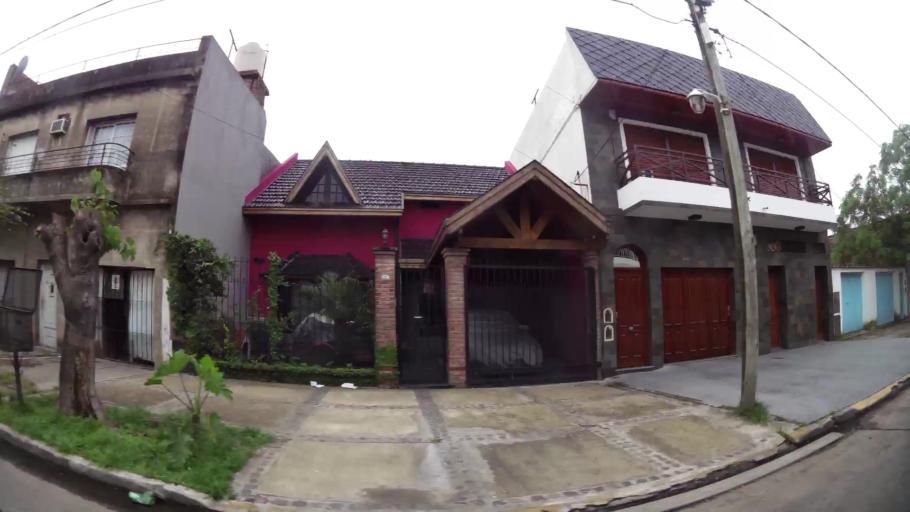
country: AR
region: Buenos Aires
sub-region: Partido de Lanus
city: Lanus
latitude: -34.7110
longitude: -58.3533
